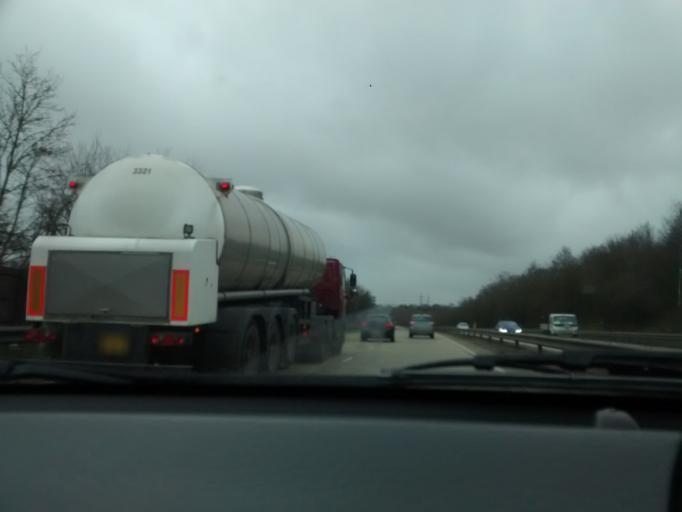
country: GB
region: England
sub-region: Suffolk
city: Bramford
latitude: 52.0711
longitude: 1.1107
